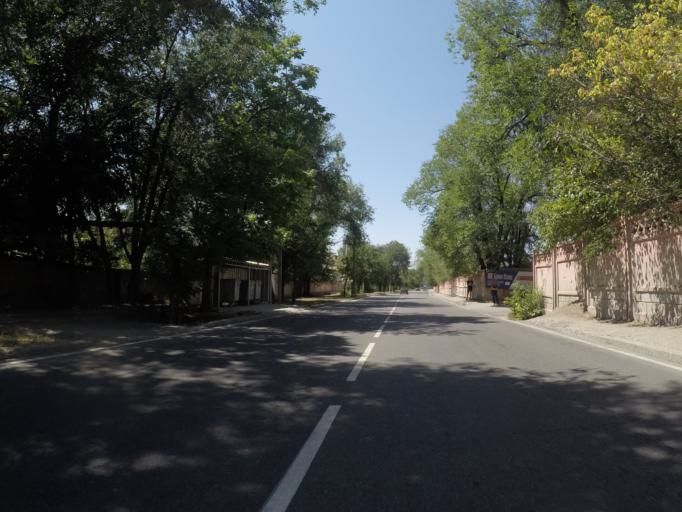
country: KG
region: Chuy
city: Bishkek
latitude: 42.8041
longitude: 74.5773
